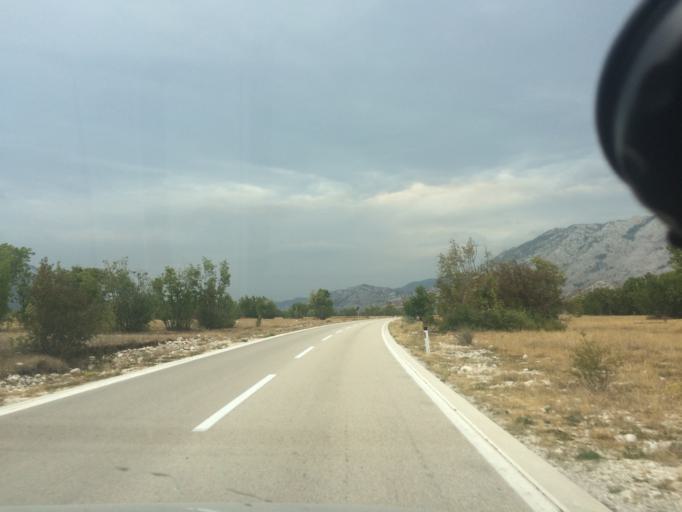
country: ME
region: Kotor
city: Risan
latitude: 42.5854
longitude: 18.6864
